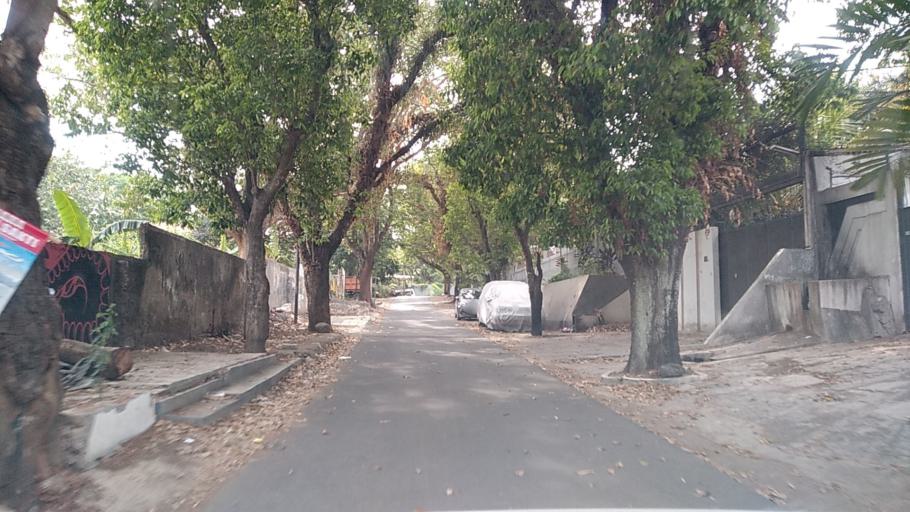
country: ID
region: Central Java
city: Semarang
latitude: -7.0085
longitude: 110.4182
